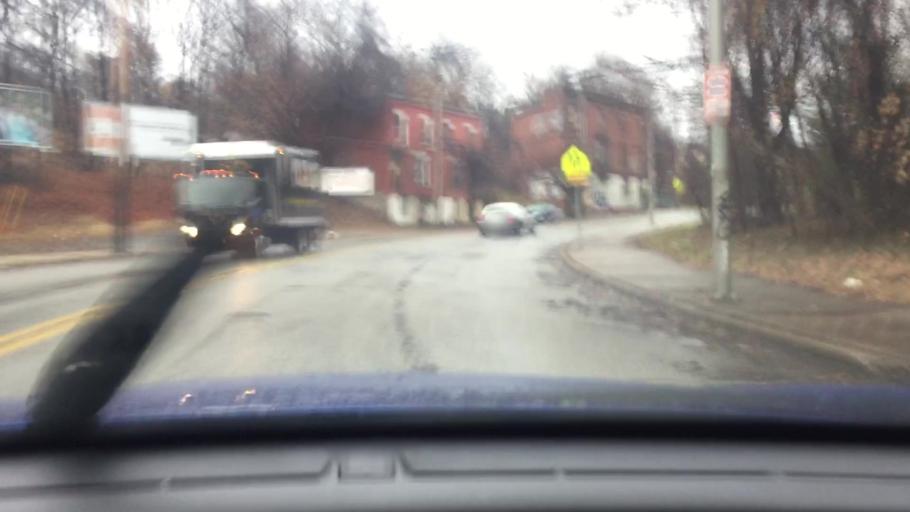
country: US
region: Pennsylvania
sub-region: Allegheny County
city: Bloomfield
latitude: 40.4499
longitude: -79.9653
